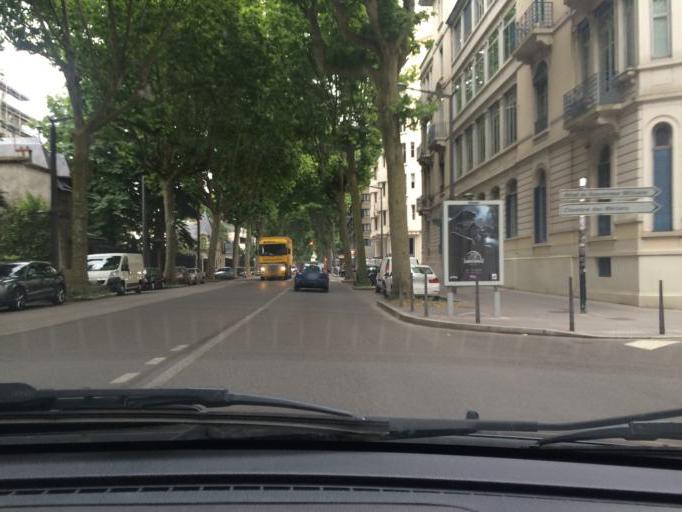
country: FR
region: Rhone-Alpes
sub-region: Departement du Rhone
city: Caluire-et-Cuire
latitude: 45.7758
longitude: 4.8460
